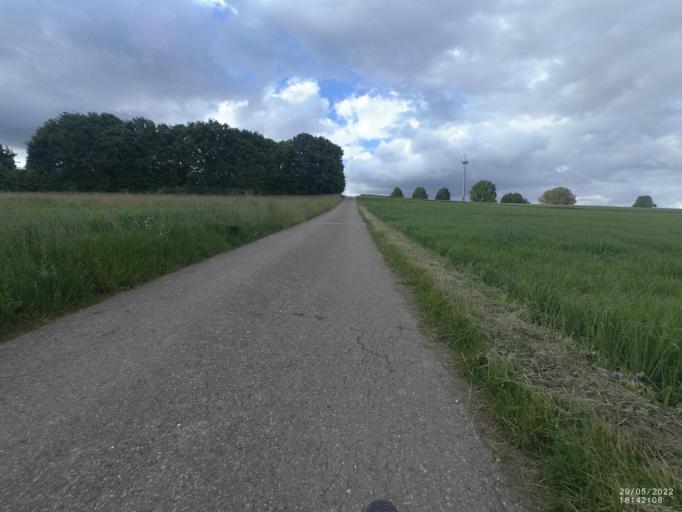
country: DE
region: Baden-Wuerttemberg
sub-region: Regierungsbezirk Stuttgart
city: Bolheim
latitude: 48.6003
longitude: 10.1071
